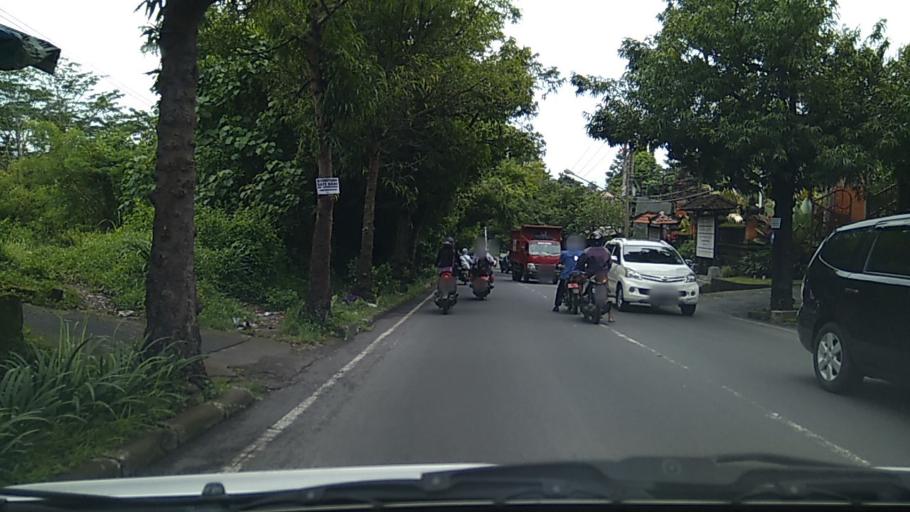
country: ID
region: Bali
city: Banjar Kelodan
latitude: -8.5388
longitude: 115.3436
